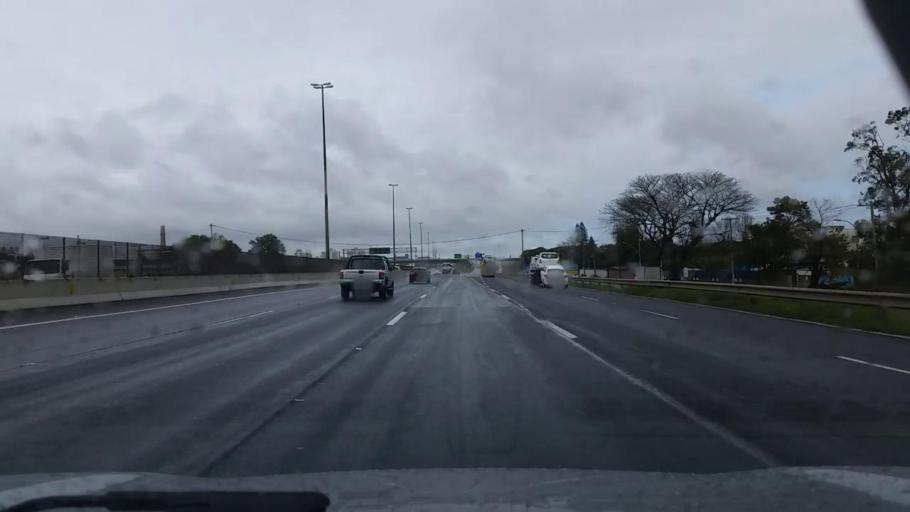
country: BR
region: Rio Grande do Sul
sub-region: Porto Alegre
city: Porto Alegre
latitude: -29.9915
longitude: -51.2046
